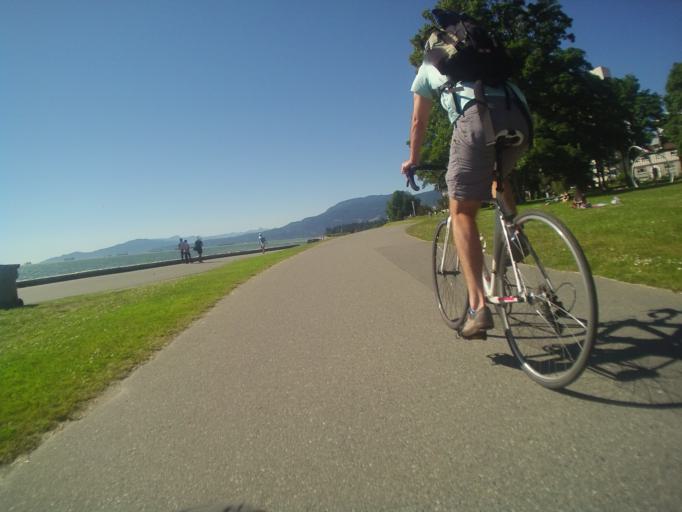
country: CA
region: British Columbia
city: West End
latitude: 49.2817
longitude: -123.1412
